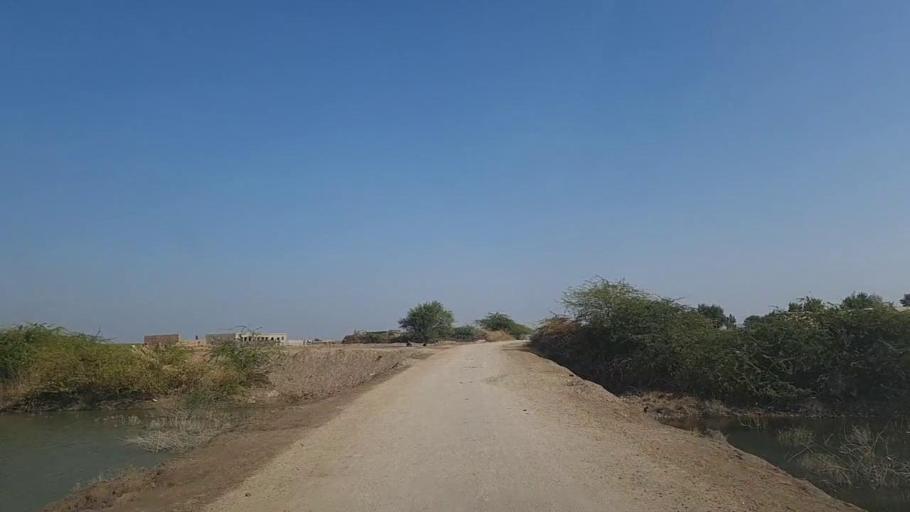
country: PK
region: Sindh
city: Digri
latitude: 25.0759
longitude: 69.2206
